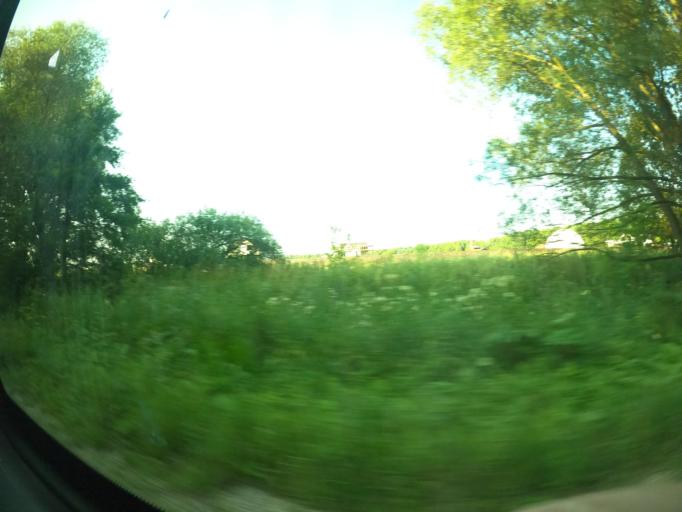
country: RU
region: Moskovskaya
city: Obolensk
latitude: 54.9423
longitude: 37.2402
